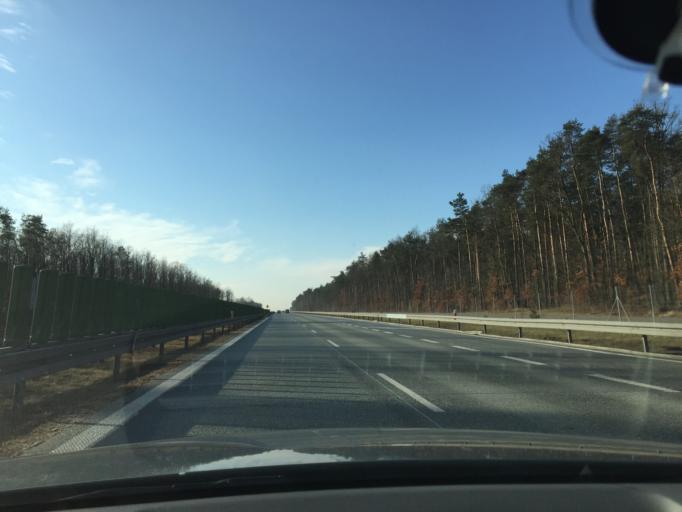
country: PL
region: Lodz Voivodeship
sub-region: Powiat rawski
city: Rawa Mazowiecka
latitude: 51.7335
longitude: 20.2304
